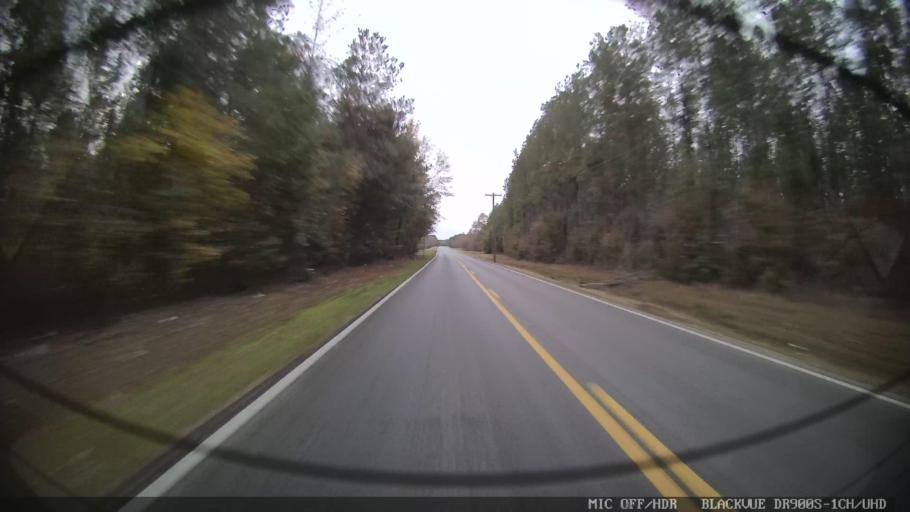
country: US
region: Mississippi
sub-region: Clarke County
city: Quitman
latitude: 32.0288
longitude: -88.8326
